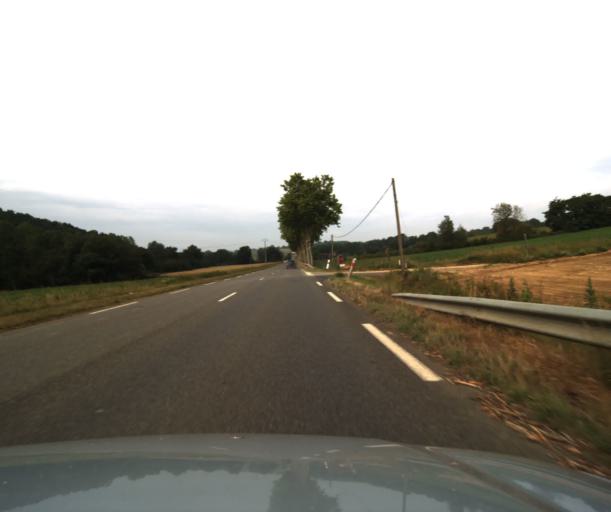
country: FR
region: Midi-Pyrenees
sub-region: Departement du Gers
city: Mirande
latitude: 43.4894
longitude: 0.3579
